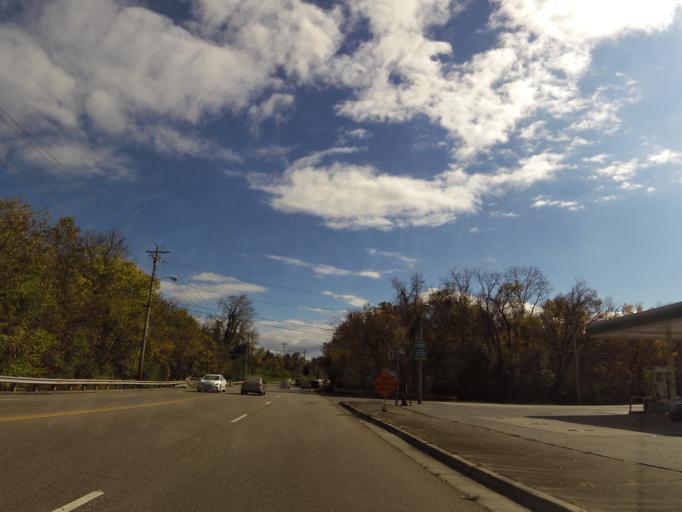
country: US
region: Tennessee
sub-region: Blount County
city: Maryville
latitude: 35.7701
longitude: -83.9835
